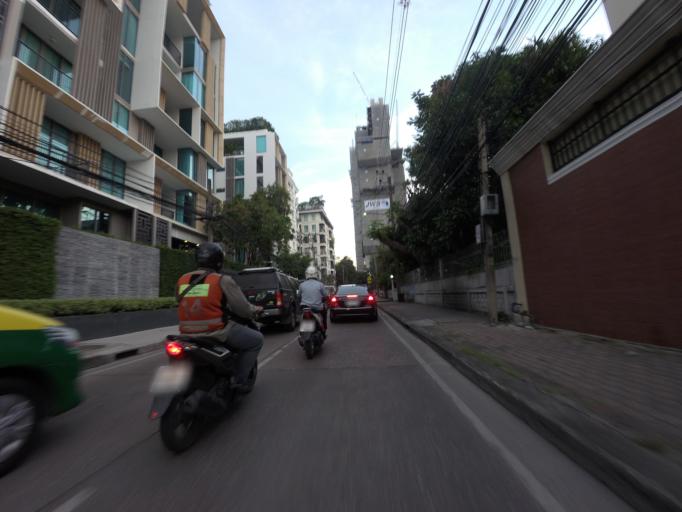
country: TH
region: Bangkok
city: Watthana
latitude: 13.7393
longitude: 100.5725
